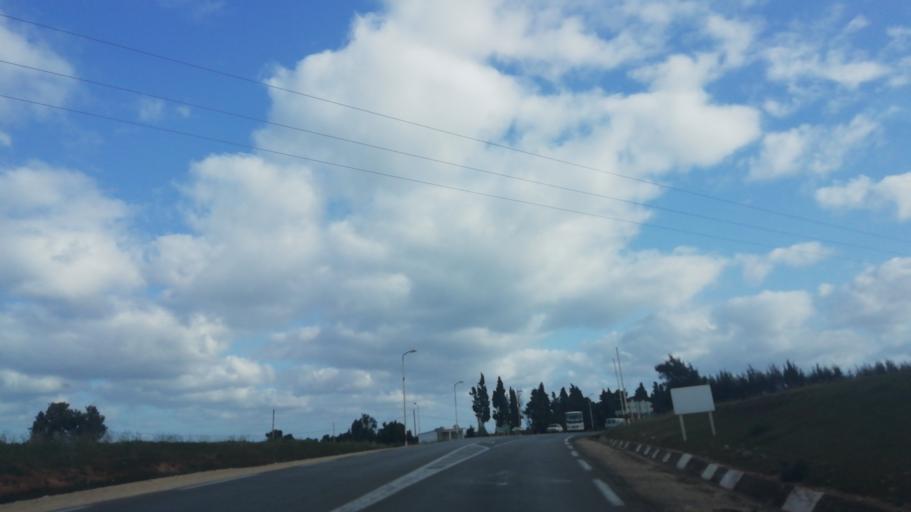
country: DZ
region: Relizane
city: Mazouna
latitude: 36.2444
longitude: 0.5368
